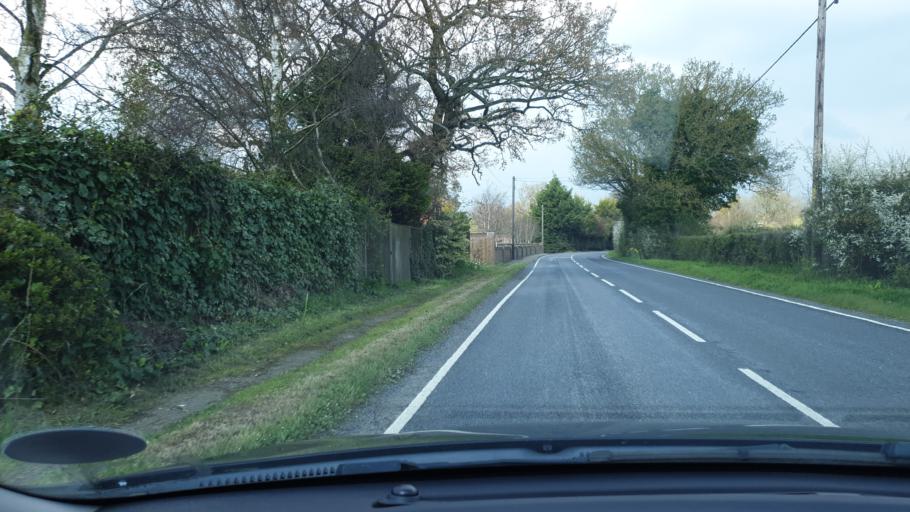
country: GB
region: England
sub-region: Essex
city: Mistley
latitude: 51.8930
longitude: 1.1034
